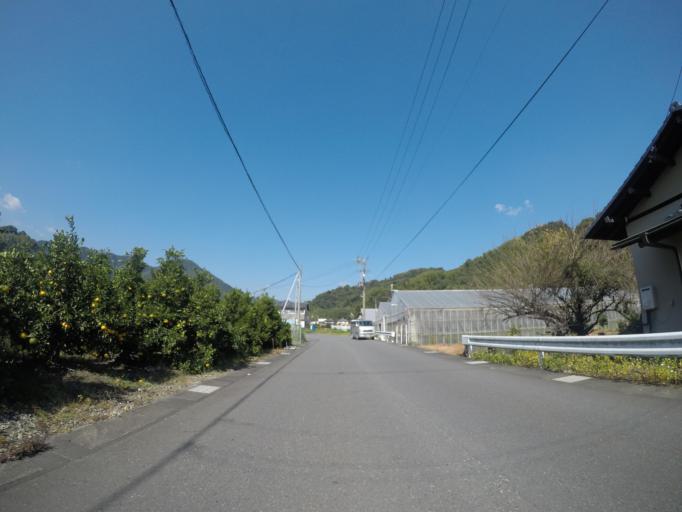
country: JP
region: Shizuoka
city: Fujinomiya
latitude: 35.0784
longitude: 138.5240
